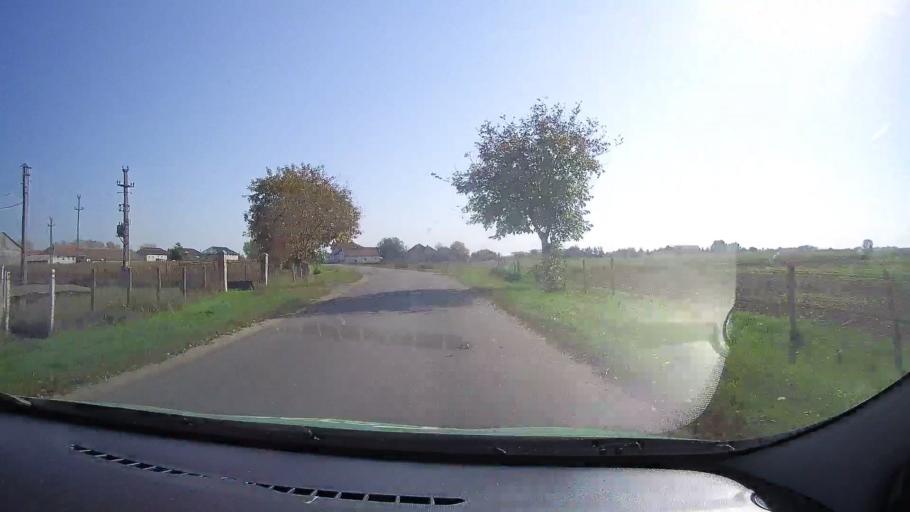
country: RO
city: Foieni
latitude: 47.6951
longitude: 22.3688
